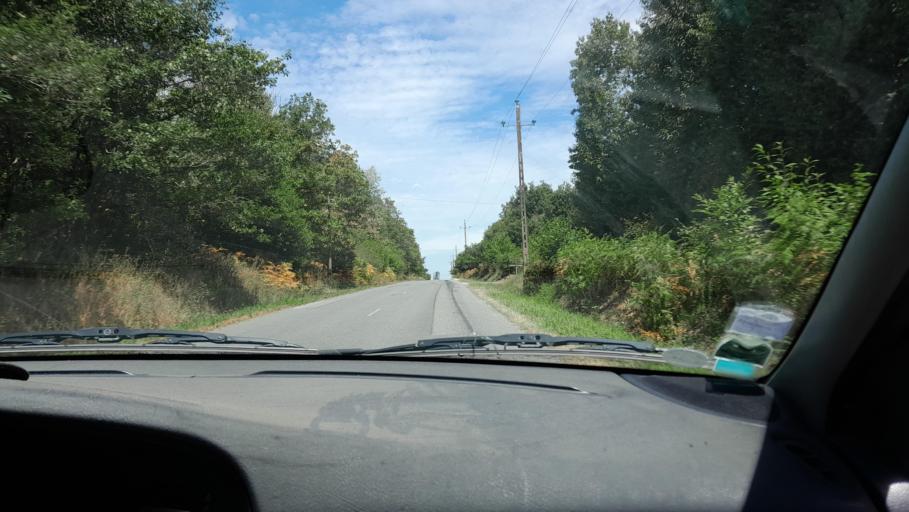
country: FR
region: Brittany
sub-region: Departement d'Ille-et-Vilaine
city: Le Pertre
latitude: 48.0072
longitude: -1.0389
